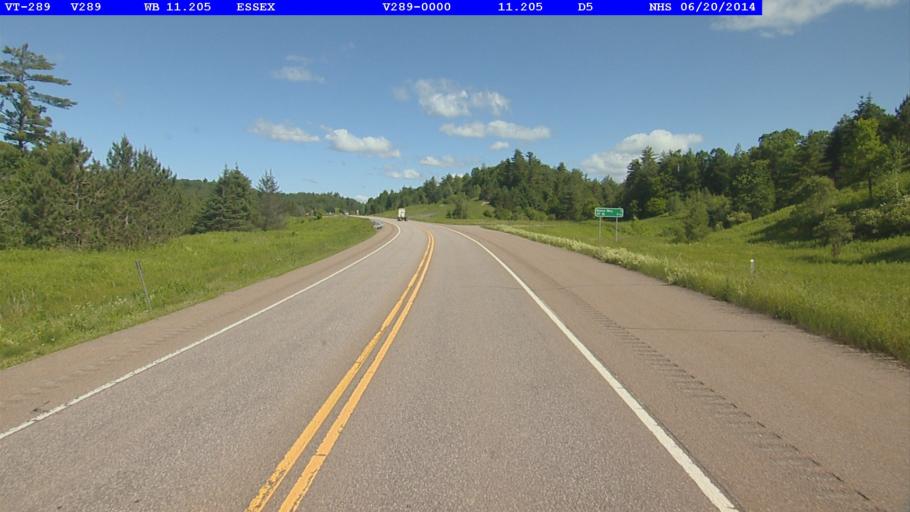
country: US
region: Vermont
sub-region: Chittenden County
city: Essex Junction
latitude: 44.4915
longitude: -73.0642
